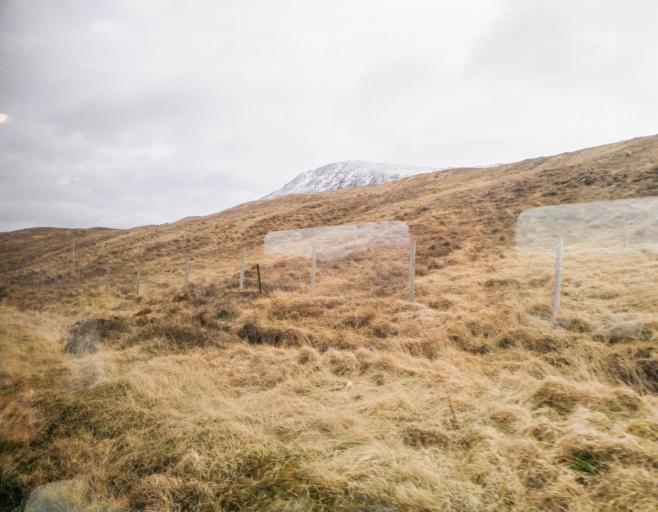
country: GB
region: Scotland
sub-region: Highland
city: Spean Bridge
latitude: 56.5491
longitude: -4.7506
